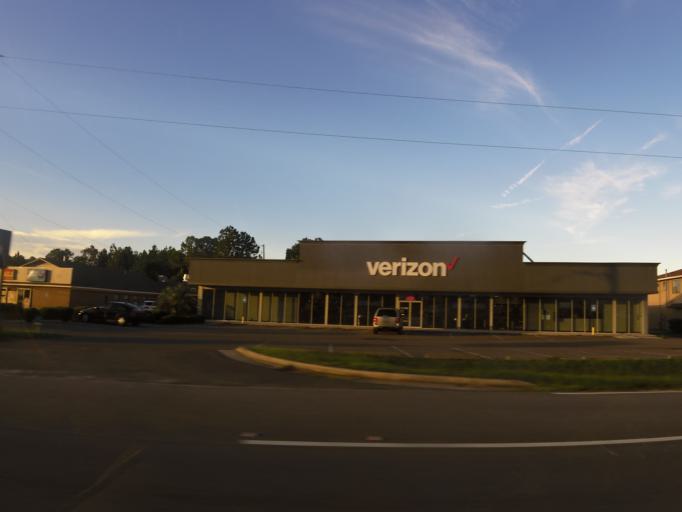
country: US
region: Georgia
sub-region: Camden County
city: Kingsland
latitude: 30.7874
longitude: -81.6482
